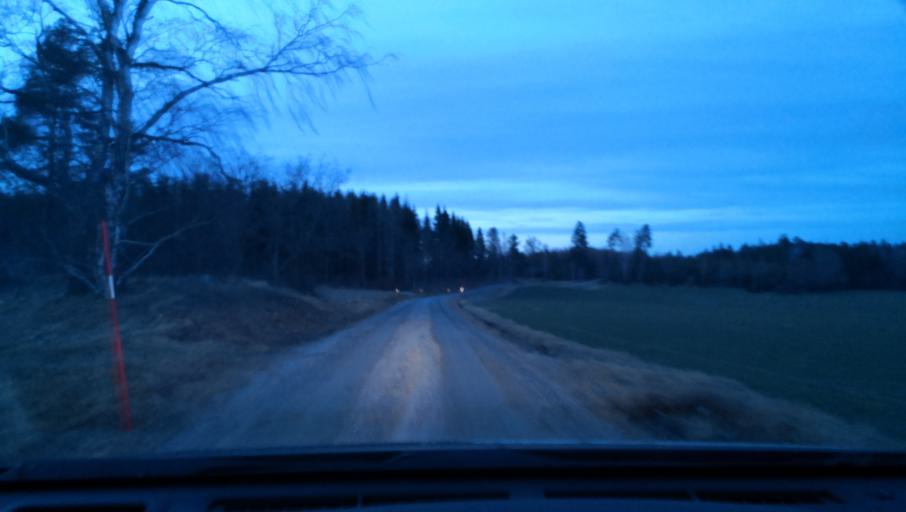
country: SE
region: Uppsala
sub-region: Enkopings Kommun
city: Dalby
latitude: 59.5594
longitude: 17.3711
